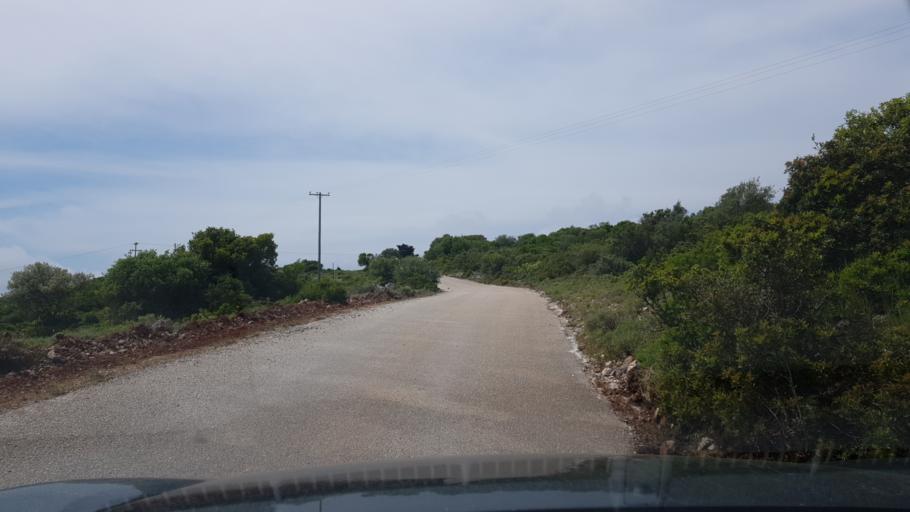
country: GR
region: Ionian Islands
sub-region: Lefkada
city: Nidri
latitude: 38.6096
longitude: 20.5662
